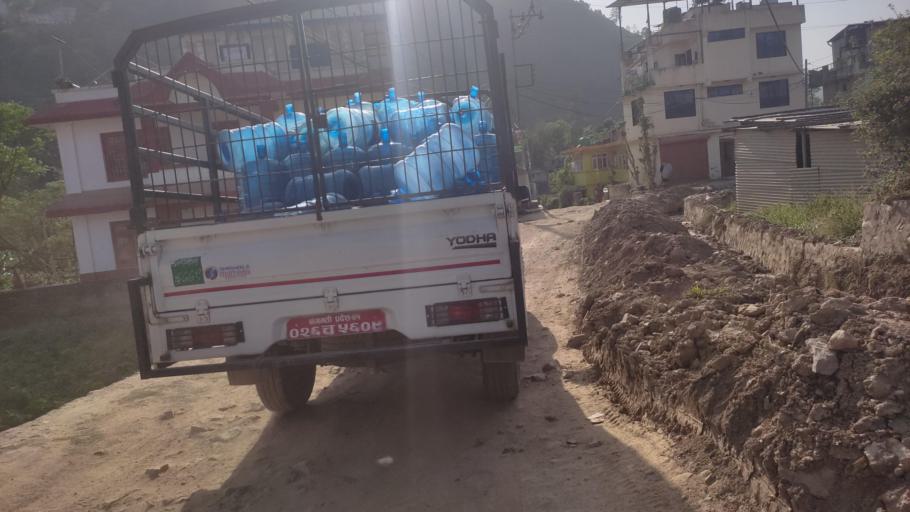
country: NP
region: Central Region
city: Kirtipur
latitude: 27.6529
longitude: 85.2756
